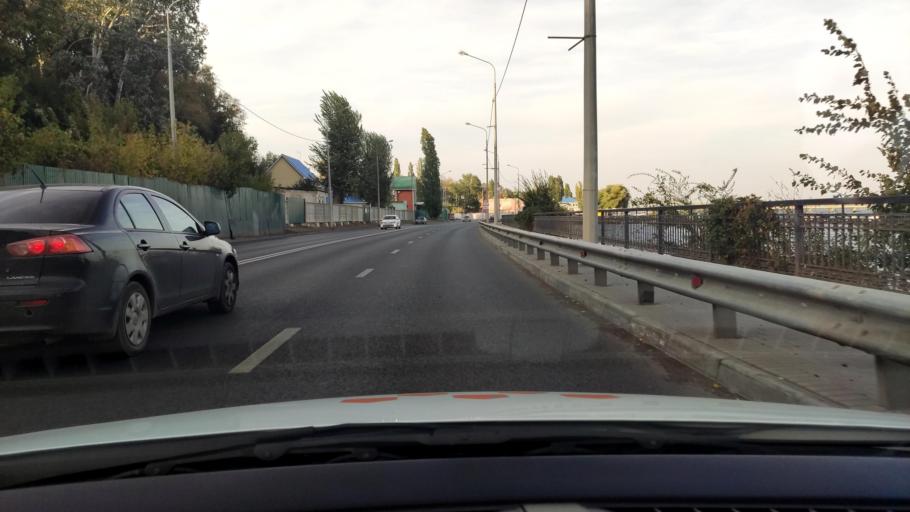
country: RU
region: Voronezj
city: Voronezh
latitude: 51.6825
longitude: 39.2281
